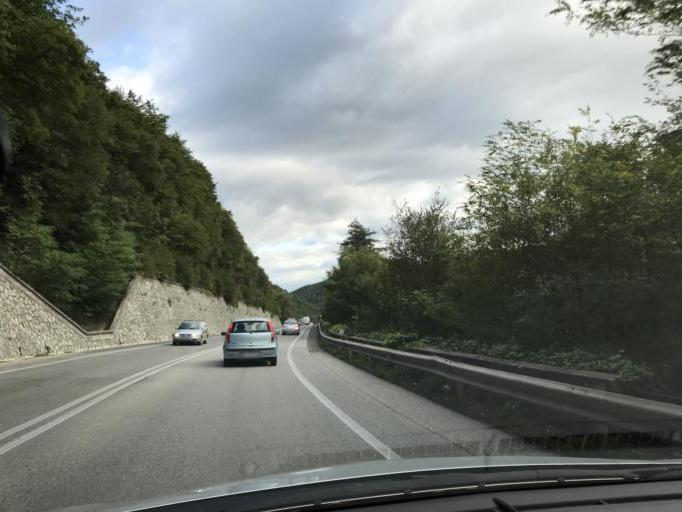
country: IT
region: Umbria
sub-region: Provincia di Perugia
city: Spoleto
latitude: 42.6917
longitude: 12.7211
